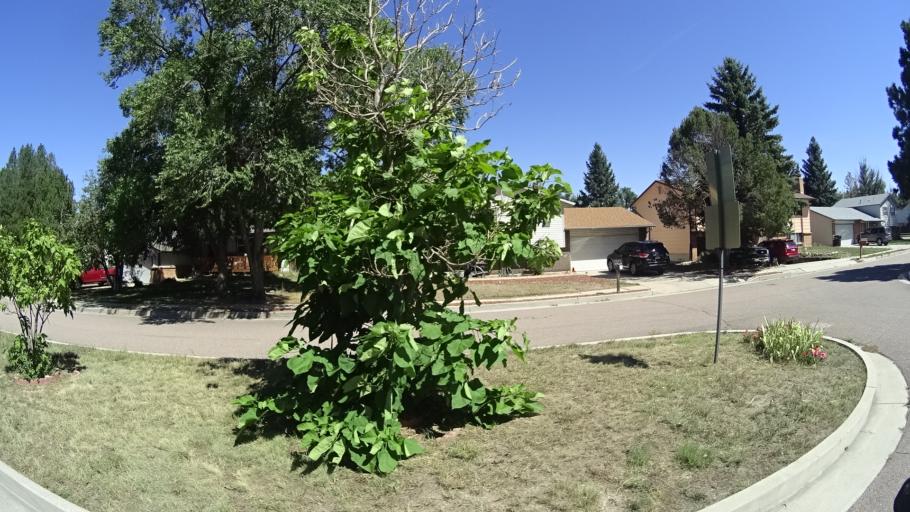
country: US
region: Colorado
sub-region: El Paso County
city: Air Force Academy
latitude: 38.9280
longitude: -104.7909
